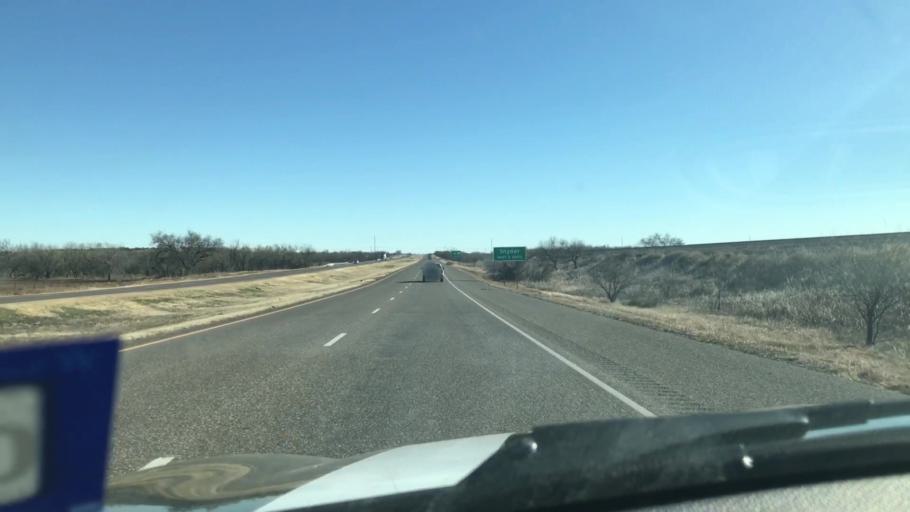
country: US
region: Texas
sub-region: Scurry County
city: Snyder
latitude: 32.8143
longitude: -100.9752
